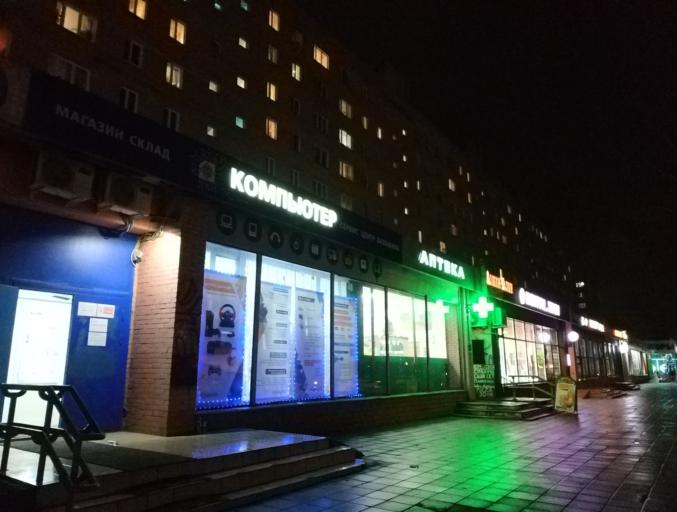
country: RU
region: Moskovskaya
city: Balashikha
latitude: 55.8177
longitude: 37.9656
